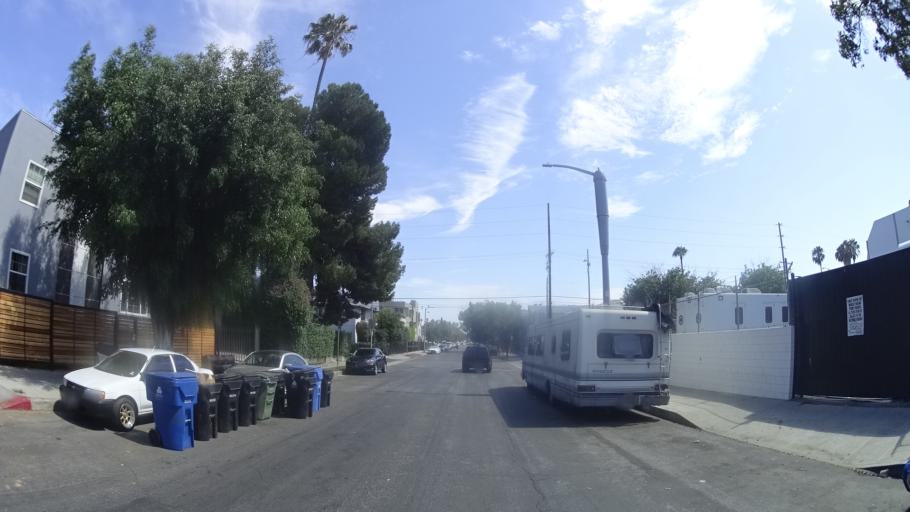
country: US
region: California
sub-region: Los Angeles County
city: Hollywood
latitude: 34.0949
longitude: -118.3200
